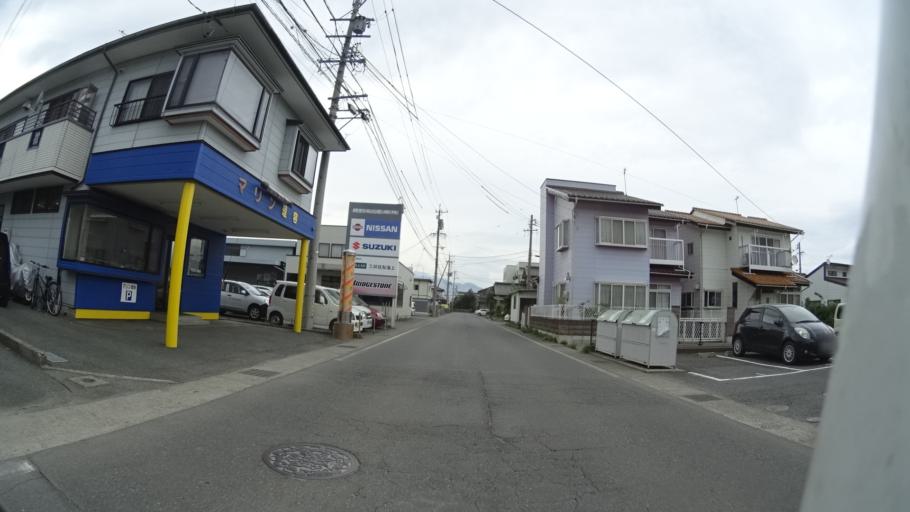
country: JP
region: Nagano
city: Nagano-shi
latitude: 36.5672
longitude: 138.1424
